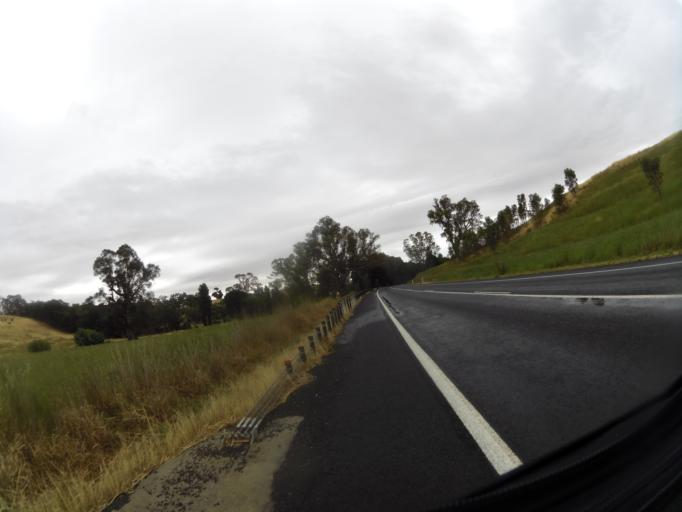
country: AU
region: Victoria
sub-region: Mount Alexander
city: Castlemaine
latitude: -37.1830
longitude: 144.0273
